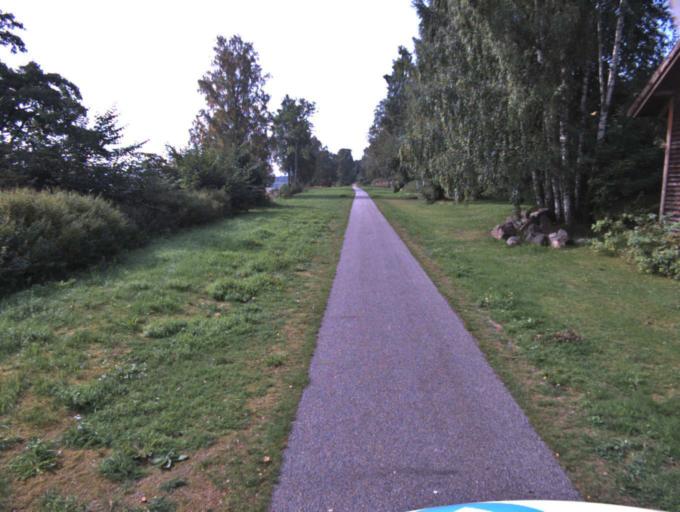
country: SE
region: Vaestra Goetaland
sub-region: Ulricehamns Kommun
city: Ulricehamn
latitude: 57.6766
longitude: 13.3740
